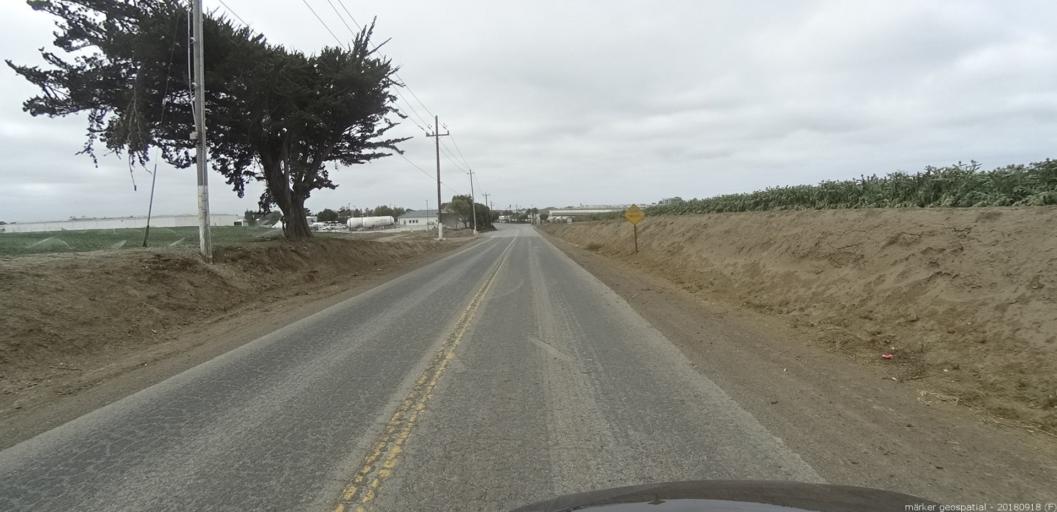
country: US
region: California
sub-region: Monterey County
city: Castroville
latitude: 36.7621
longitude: -121.7365
